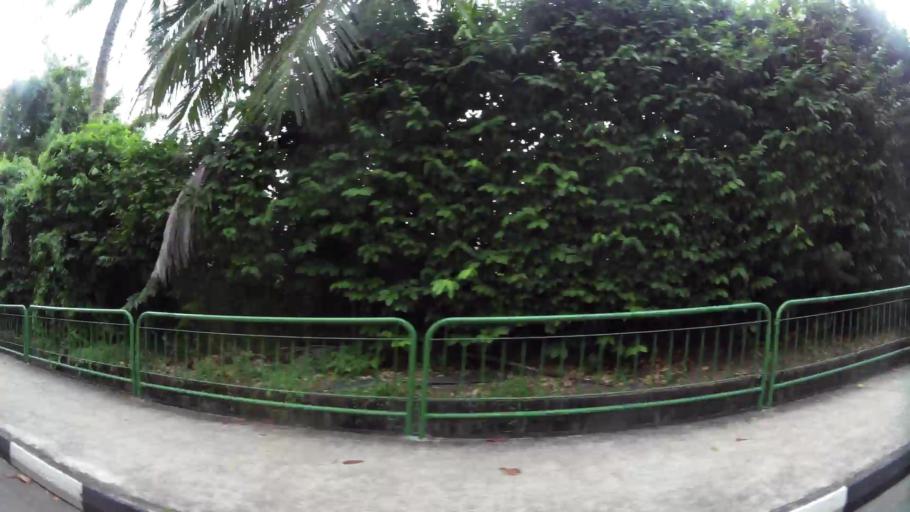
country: SG
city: Singapore
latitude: 1.2764
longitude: 103.8328
